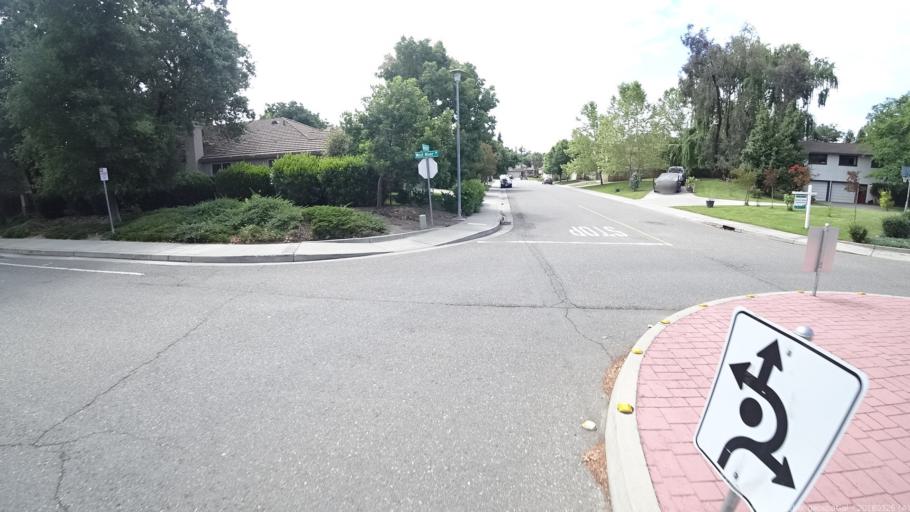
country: US
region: California
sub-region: Yolo County
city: West Sacramento
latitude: 38.6076
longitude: -121.5386
